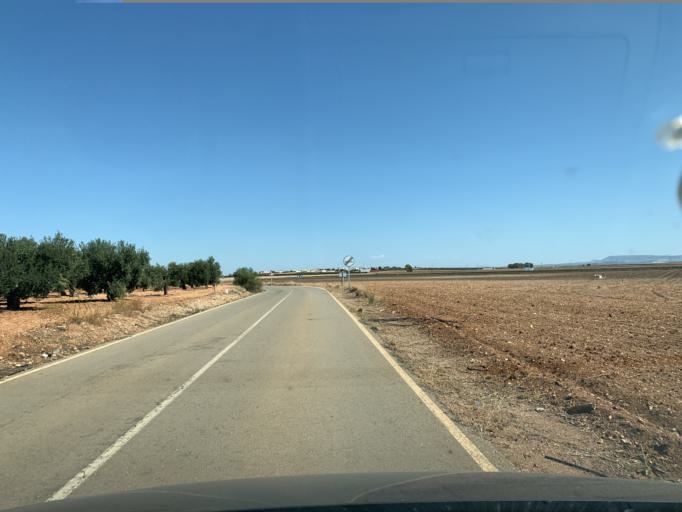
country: ES
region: Andalusia
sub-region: Provincia de Sevilla
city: La Lantejuela
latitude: 37.3453
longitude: -5.2559
